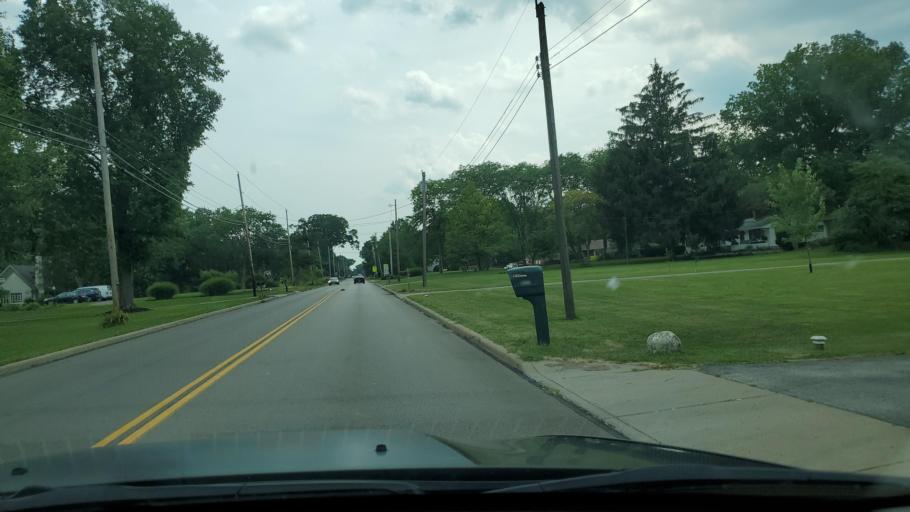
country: US
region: Ohio
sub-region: Trumbull County
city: Bolindale
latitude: 41.2311
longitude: -80.7643
